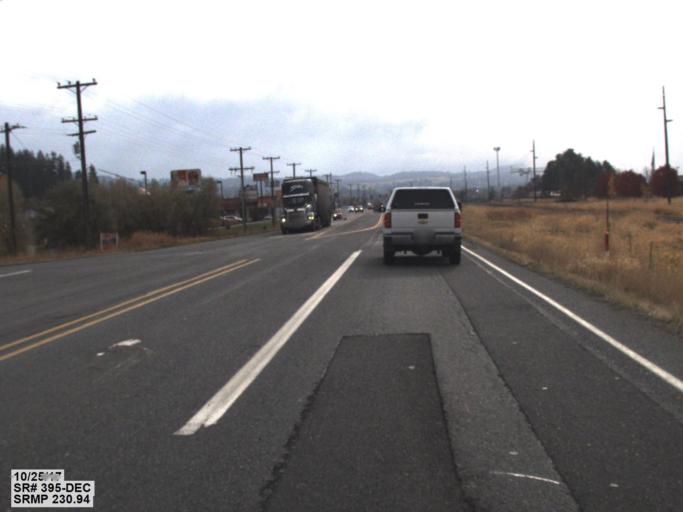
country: US
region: Washington
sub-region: Stevens County
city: Colville
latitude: 48.5584
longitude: -117.9260
